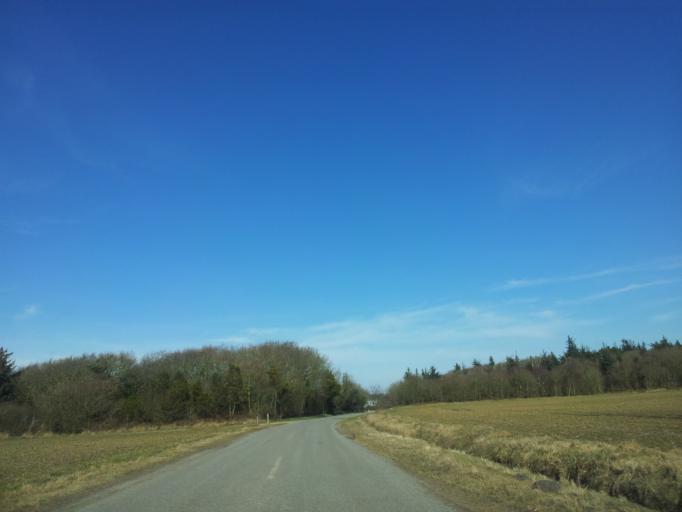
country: DK
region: South Denmark
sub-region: Tonder Kommune
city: Sherrebek
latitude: 55.1889
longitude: 8.7202
